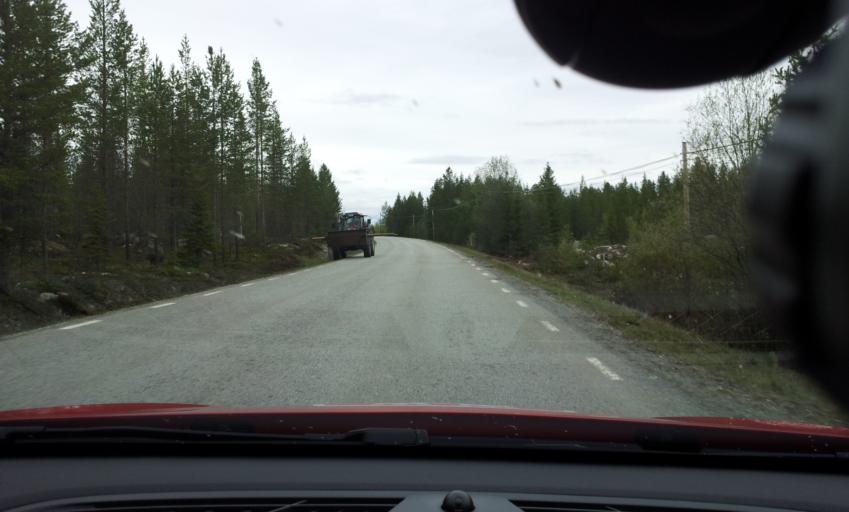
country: SE
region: Jaemtland
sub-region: Bergs Kommun
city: Hoverberg
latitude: 62.7561
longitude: 14.5656
